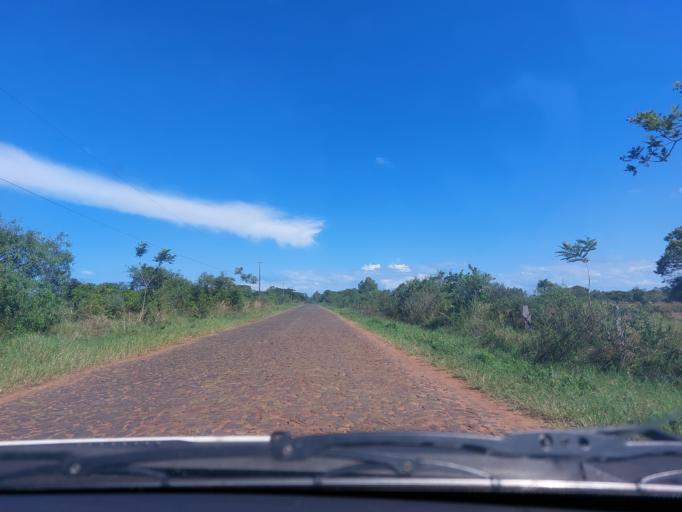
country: PY
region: San Pedro
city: Itacurubi del Rosario
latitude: -24.5854
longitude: -56.6006
